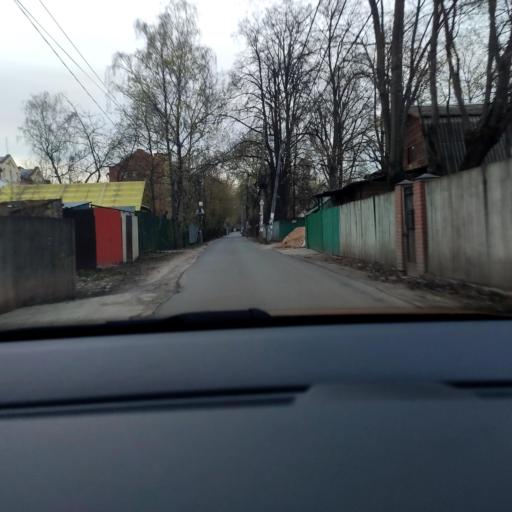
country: RU
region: Moscow
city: Yaroslavskiy
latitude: 55.8869
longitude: 37.7249
